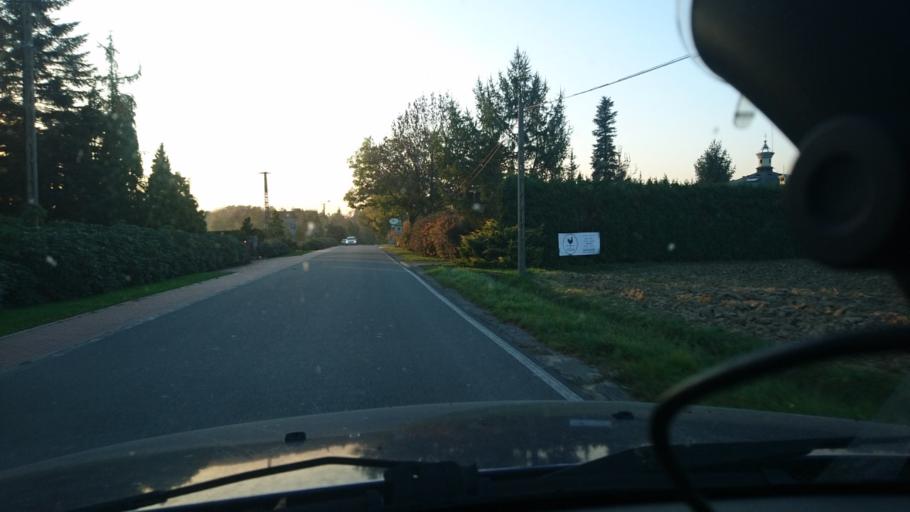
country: PL
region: Silesian Voivodeship
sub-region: Powiat bielski
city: Pisarzowice
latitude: 49.8727
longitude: 19.1483
